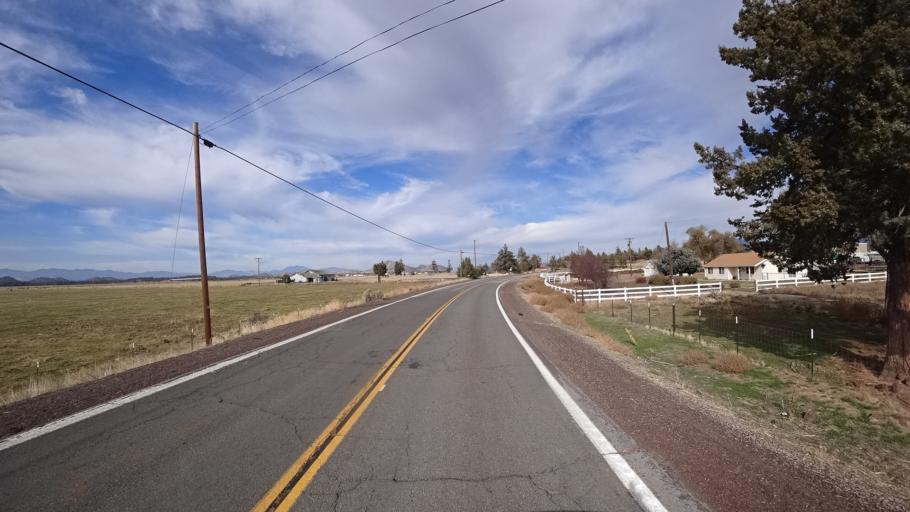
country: US
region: California
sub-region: Siskiyou County
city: Montague
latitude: 41.6102
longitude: -122.3999
